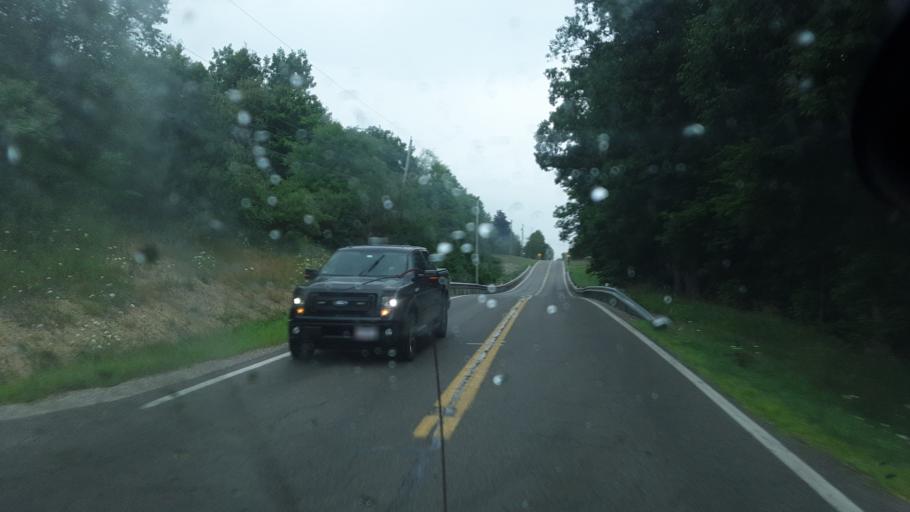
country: US
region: Ohio
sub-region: Williams County
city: Bryan
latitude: 41.4849
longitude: -84.6131
